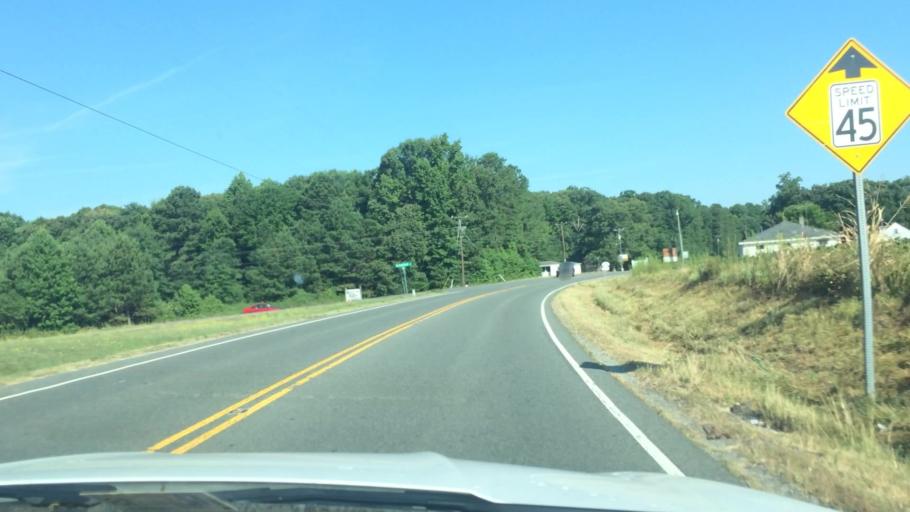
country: US
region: Virginia
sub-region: Lancaster County
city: Lancaster
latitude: 37.7705
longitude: -76.5075
